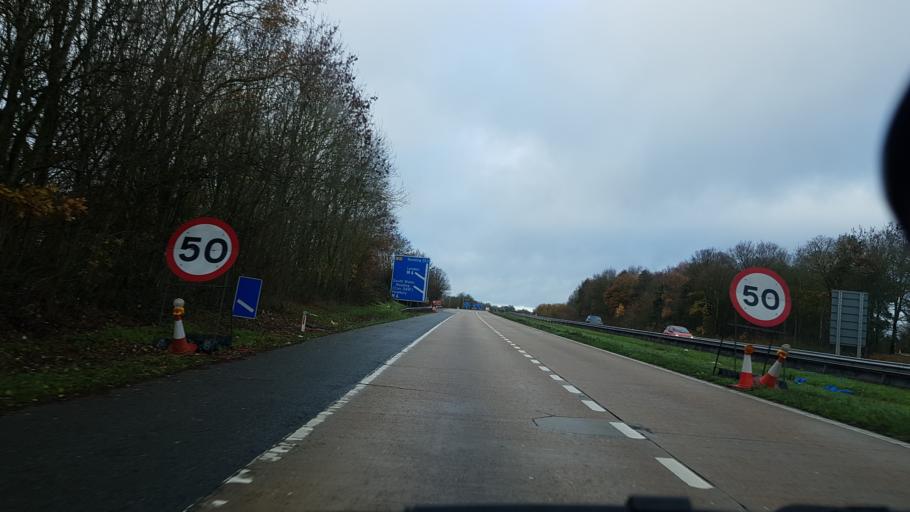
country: GB
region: England
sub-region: Wokingham
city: Wokingham
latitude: 51.4289
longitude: -0.8466
